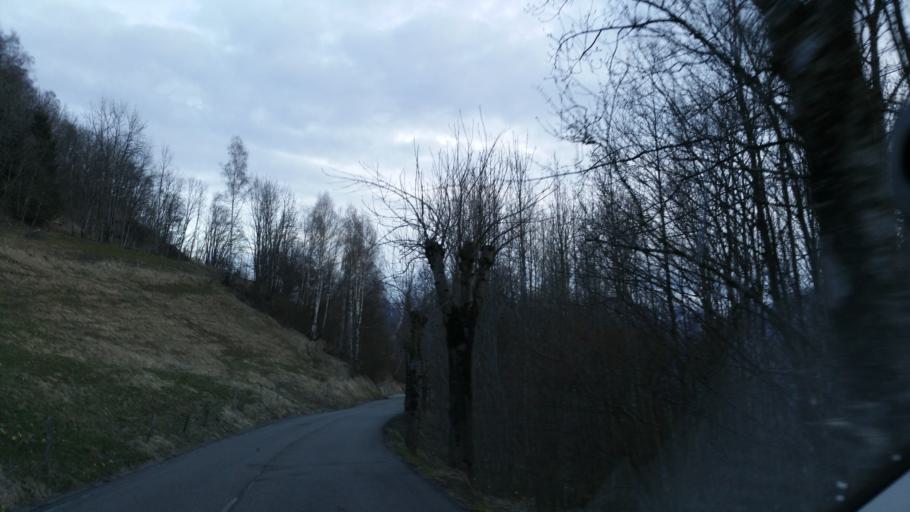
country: FR
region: Rhone-Alpes
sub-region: Departement de la Savoie
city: La Chambre
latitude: 45.3959
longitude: 6.3362
